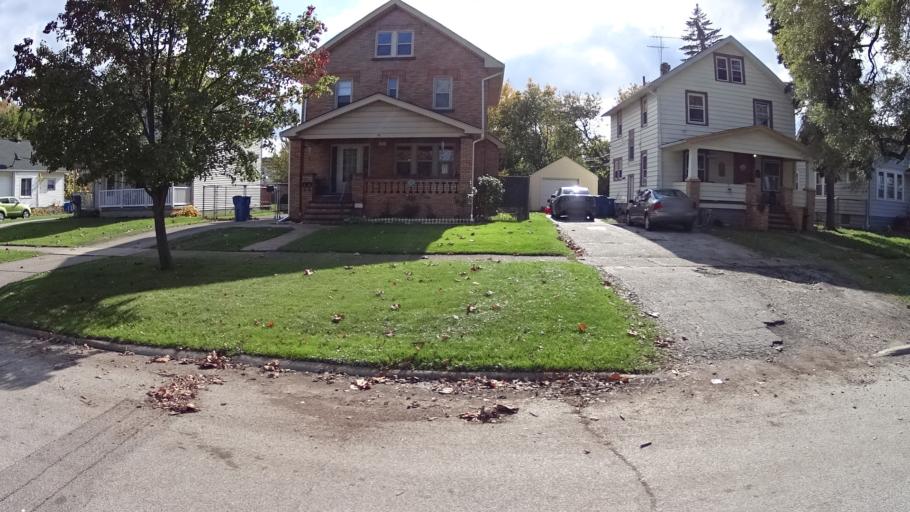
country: US
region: Ohio
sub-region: Lorain County
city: Sheffield
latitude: 41.4401
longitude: -82.1291
